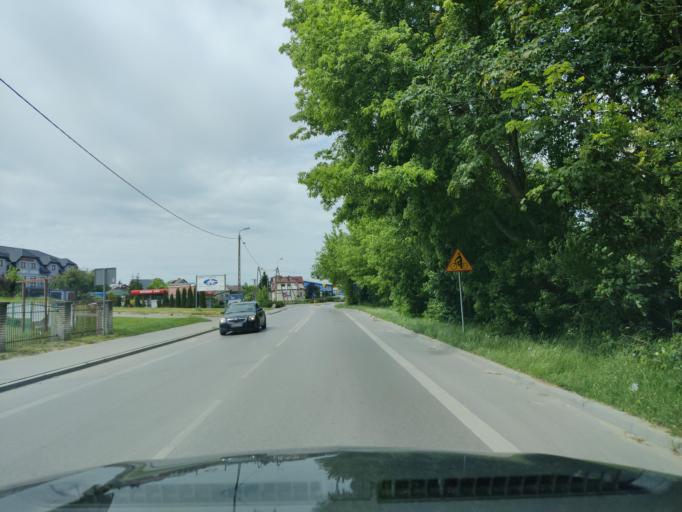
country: PL
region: Masovian Voivodeship
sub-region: Powiat pultuski
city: Pultusk
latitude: 52.6993
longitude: 21.0785
